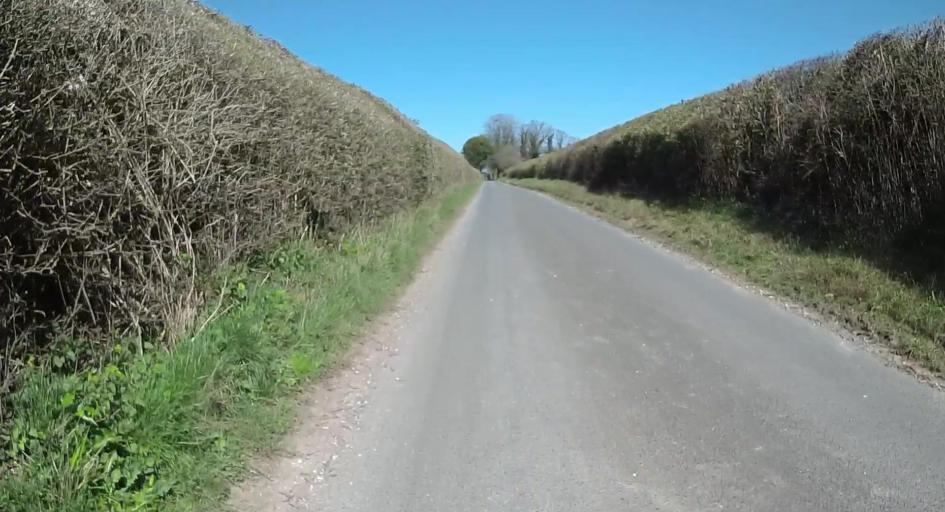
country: GB
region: England
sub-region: Hampshire
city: Kingsclere
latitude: 51.2730
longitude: -1.1920
